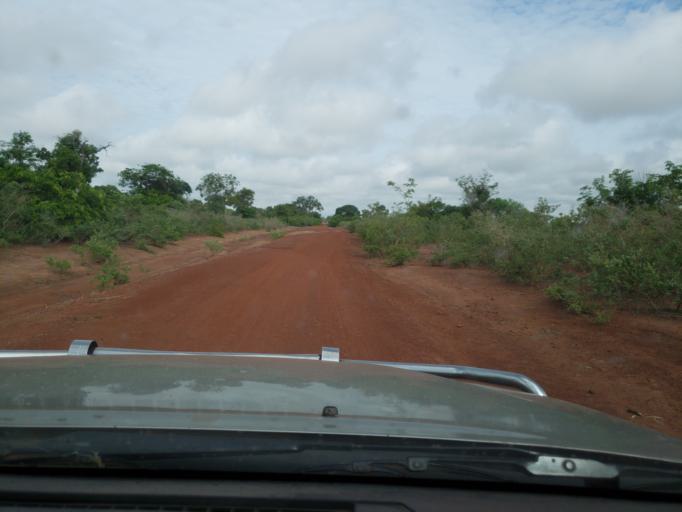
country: ML
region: Sikasso
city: Koutiala
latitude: 12.3925
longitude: -6.0025
